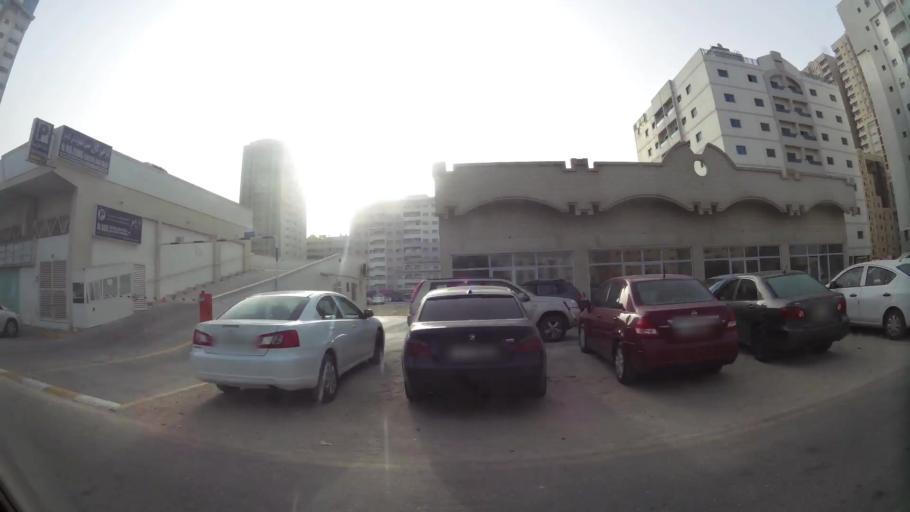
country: AE
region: Ash Shariqah
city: Sharjah
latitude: 25.3419
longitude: 55.4019
